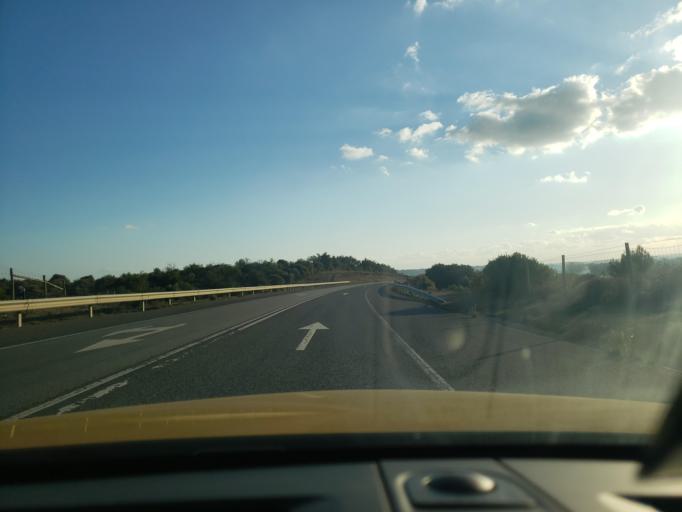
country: PT
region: Faro
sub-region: Portimao
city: Portimao
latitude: 37.1714
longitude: -8.5673
